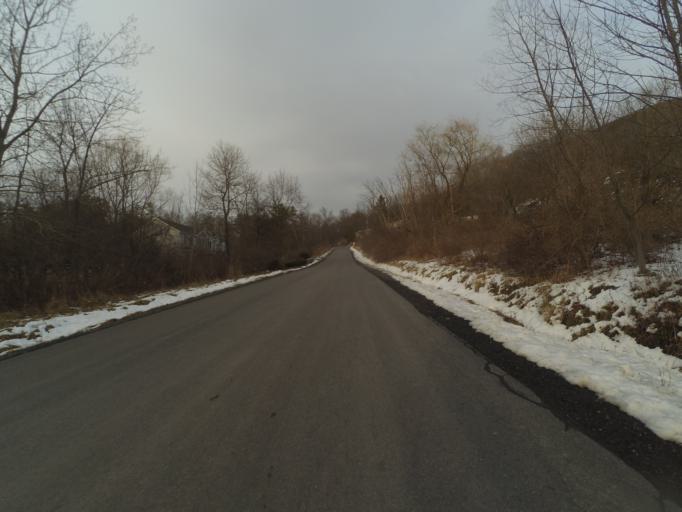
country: US
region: Pennsylvania
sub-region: Centre County
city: Lemont
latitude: 40.8091
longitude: -77.8090
